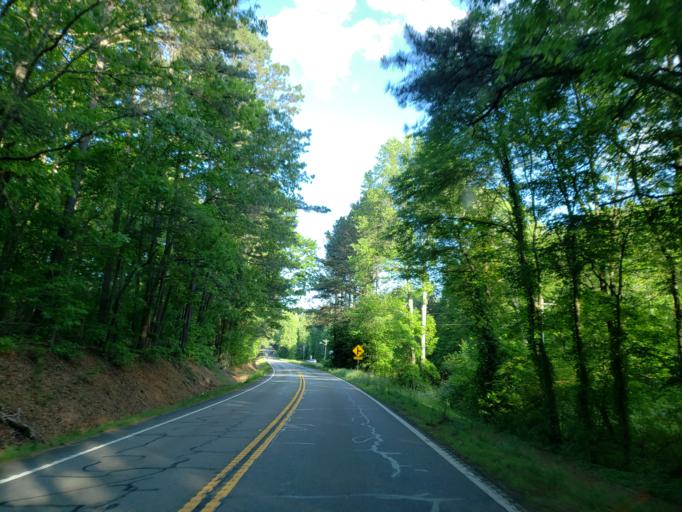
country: US
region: Georgia
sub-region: Cherokee County
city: Canton
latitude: 34.3411
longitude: -84.5761
